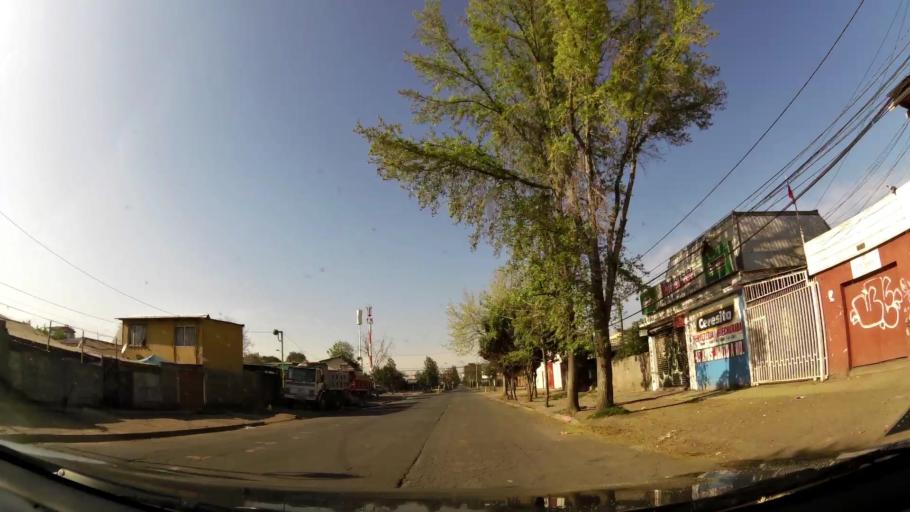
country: CL
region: Santiago Metropolitan
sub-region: Provincia de Santiago
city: Santiago
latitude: -33.3855
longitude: -70.6671
